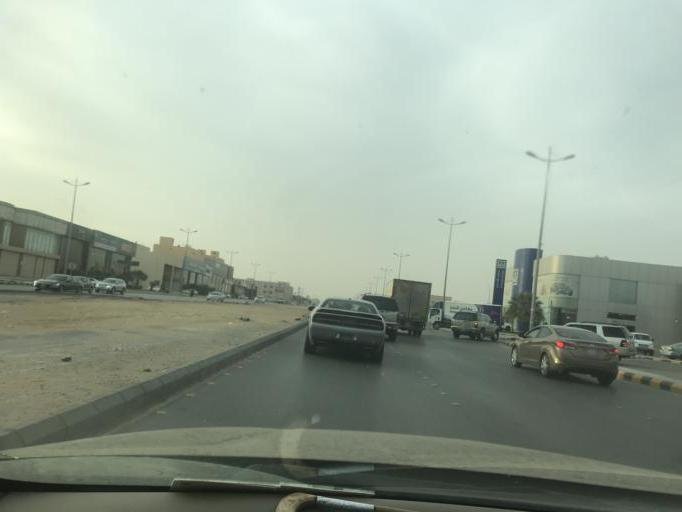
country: SA
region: Ar Riyad
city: Riyadh
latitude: 24.8041
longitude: 46.7384
